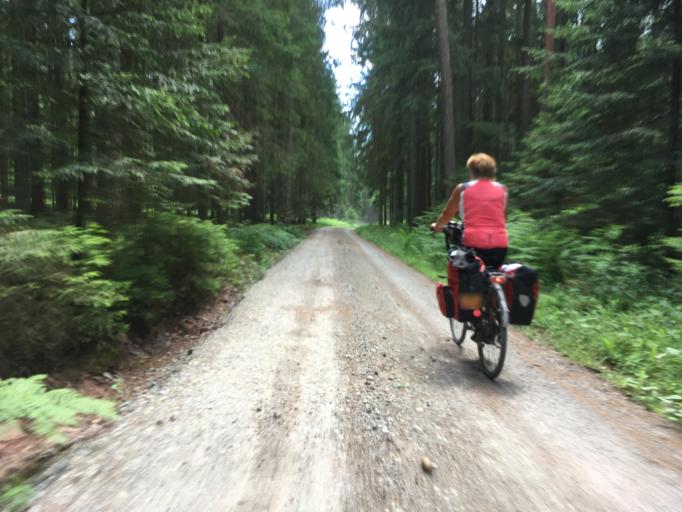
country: DE
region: Baden-Wuerttemberg
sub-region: Karlsruhe Region
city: Baiersbronn
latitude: 48.5502
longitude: 8.4190
